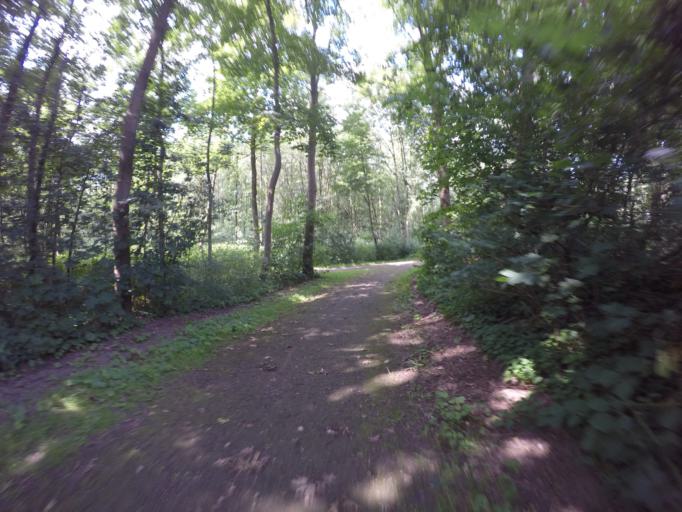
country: DE
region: North Rhine-Westphalia
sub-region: Regierungsbezirk Munster
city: Borken
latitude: 51.8549
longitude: 6.8591
